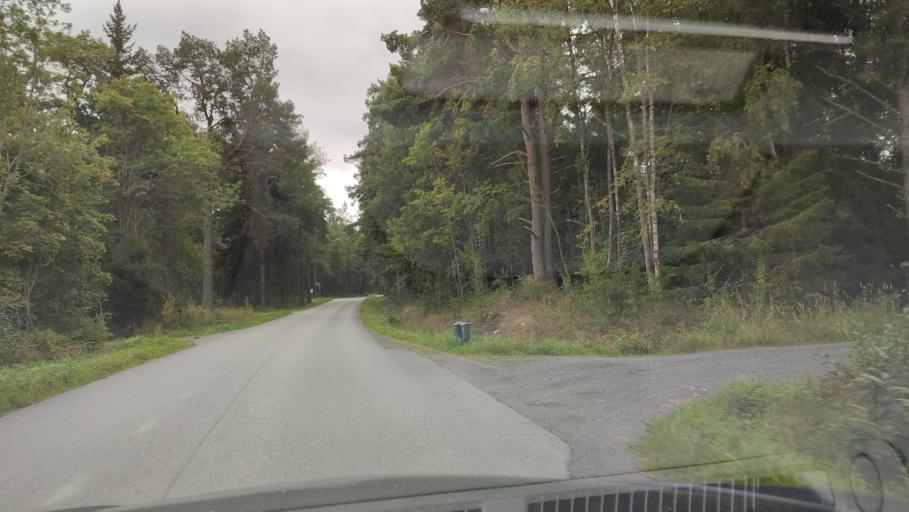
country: FI
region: Ostrobothnia
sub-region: Sydosterbotten
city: Kristinestad
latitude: 62.2592
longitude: 21.3588
